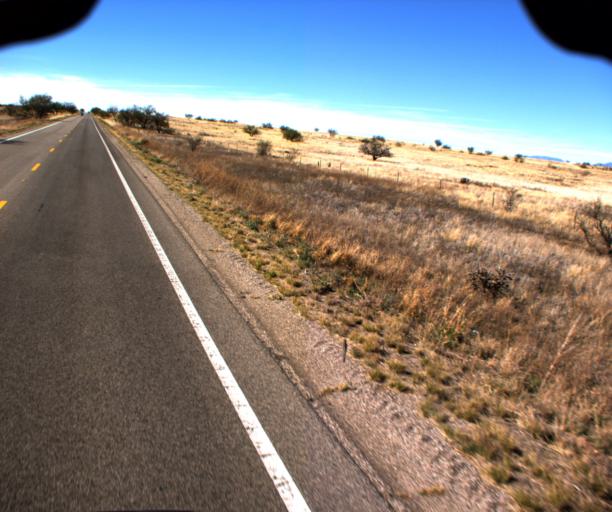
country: US
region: Arizona
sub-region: Pima County
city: Corona de Tucson
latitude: 31.7548
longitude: -110.6740
